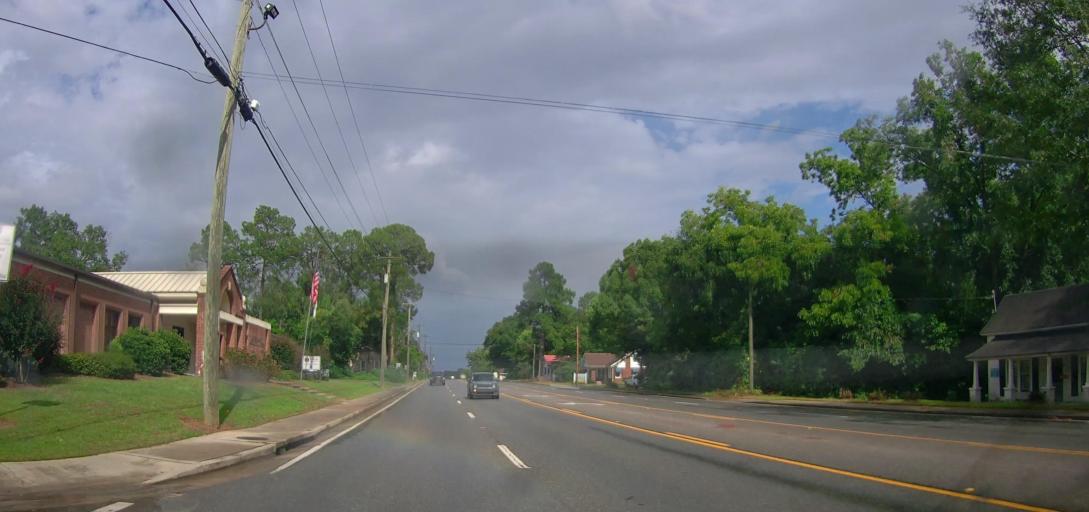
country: US
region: Georgia
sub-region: Coffee County
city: Douglas
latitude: 31.5087
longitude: -82.8417
